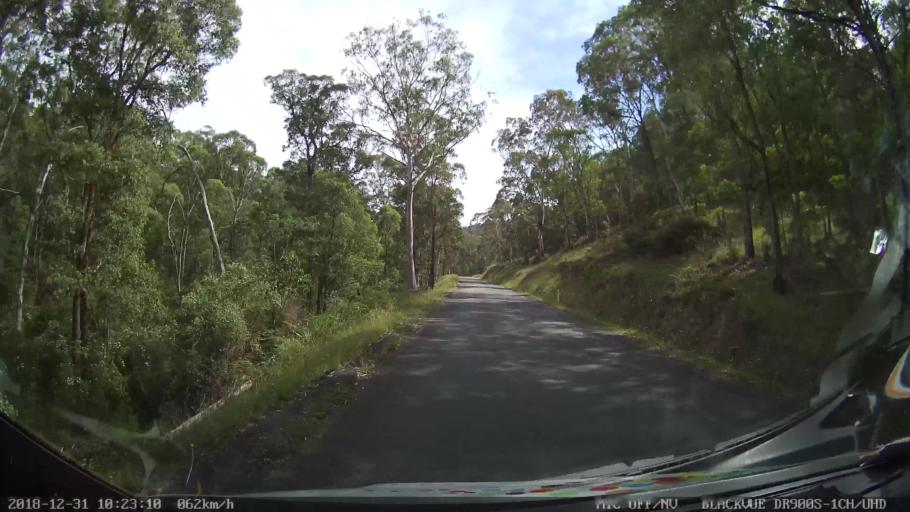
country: AU
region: New South Wales
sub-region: Snowy River
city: Jindabyne
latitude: -36.5192
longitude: 148.1436
